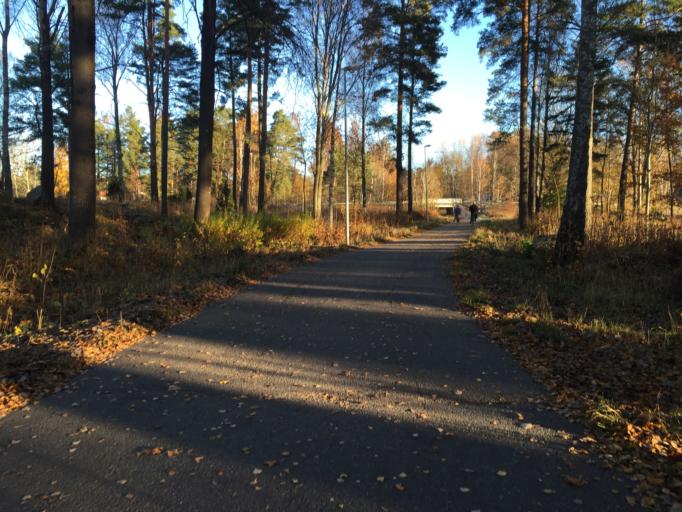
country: SE
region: Vaestmanland
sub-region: Hallstahammars Kommun
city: Hallstahammar
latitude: 59.6246
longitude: 16.2383
